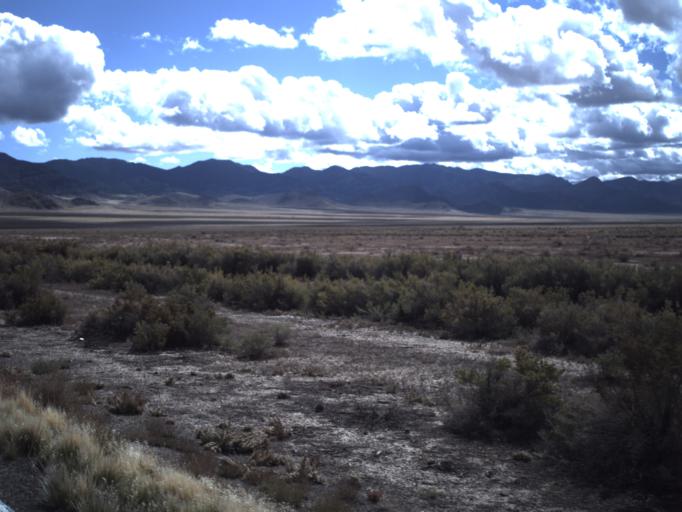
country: US
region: Utah
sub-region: Beaver County
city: Milford
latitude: 38.5249
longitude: -113.6618
